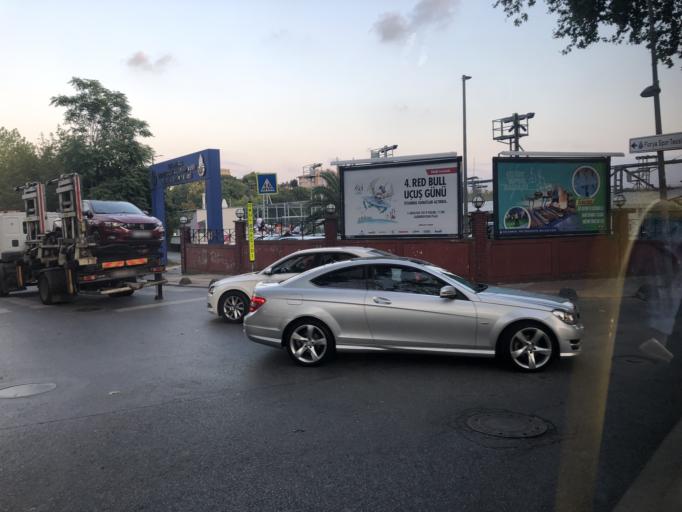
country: TR
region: Istanbul
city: Bahcelievler
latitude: 40.9758
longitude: 28.7909
